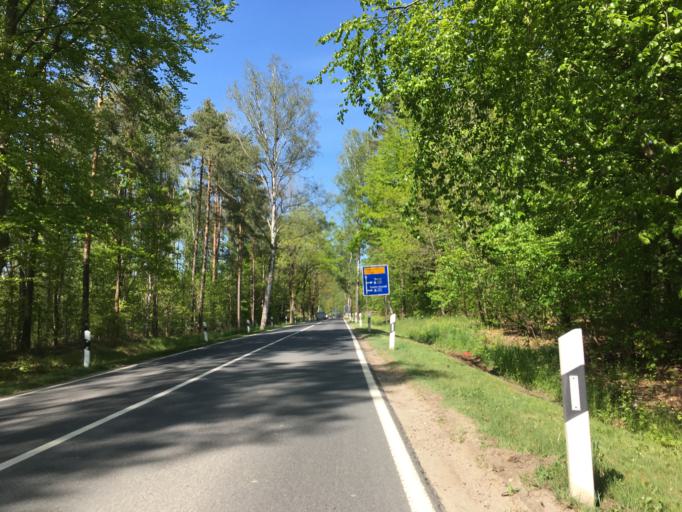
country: DE
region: Brandenburg
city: Rudnitz
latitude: 52.7688
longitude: 13.5650
